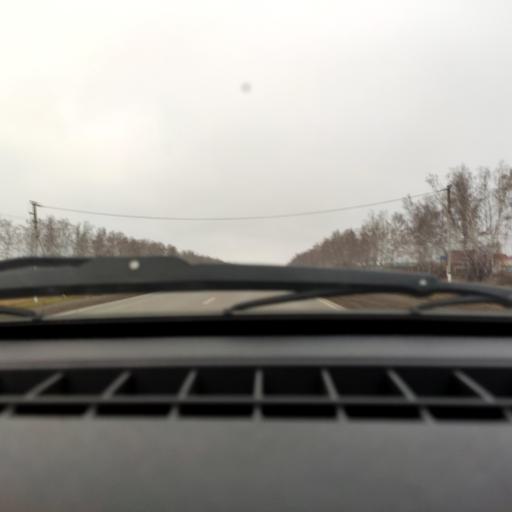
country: RU
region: Bashkortostan
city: Chishmy
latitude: 54.6092
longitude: 55.3813
